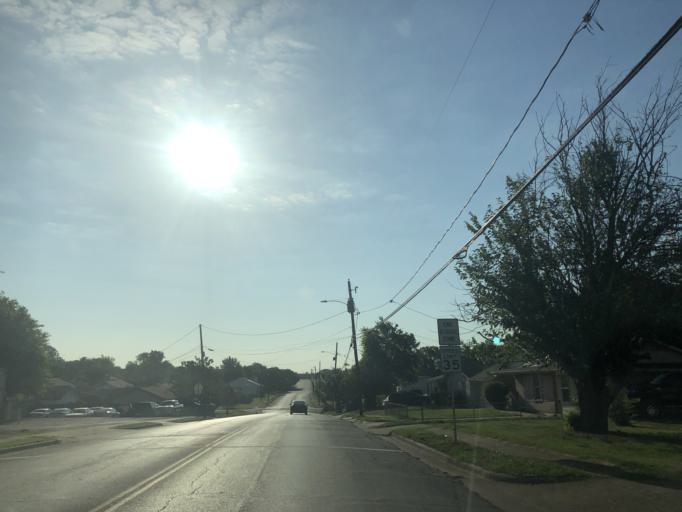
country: US
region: Texas
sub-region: Dallas County
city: Grand Prairie
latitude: 32.7350
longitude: -97.0288
